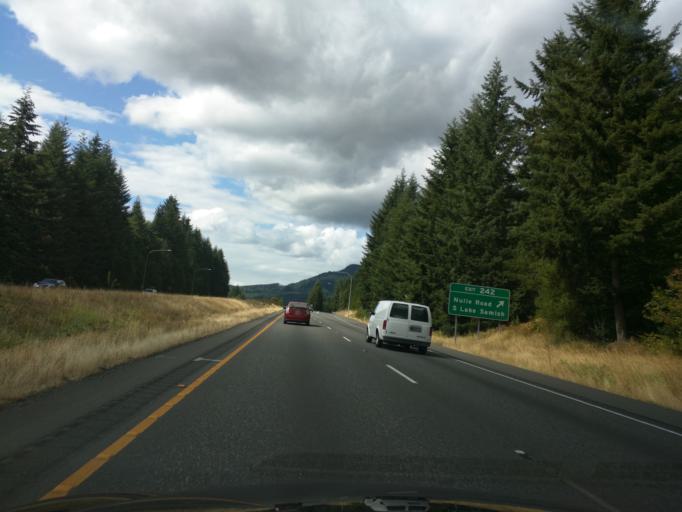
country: US
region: Washington
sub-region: Whatcom County
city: Sudden Valley
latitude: 48.6435
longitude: -122.3637
